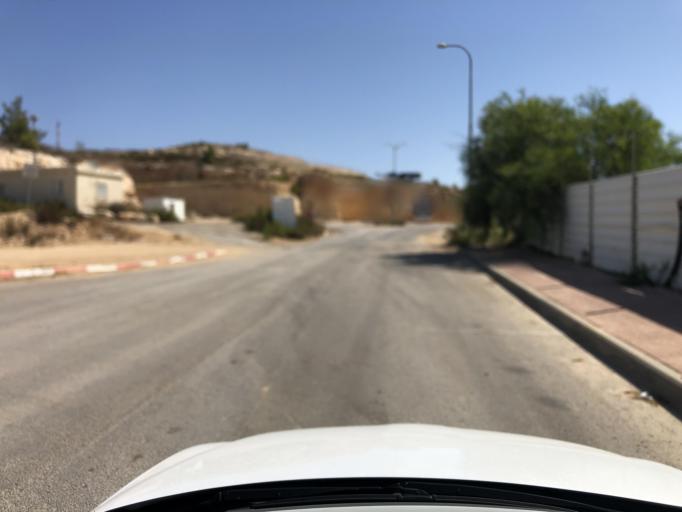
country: PS
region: West Bank
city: An Nabi Ilyas
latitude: 32.1637
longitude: 35.0236
